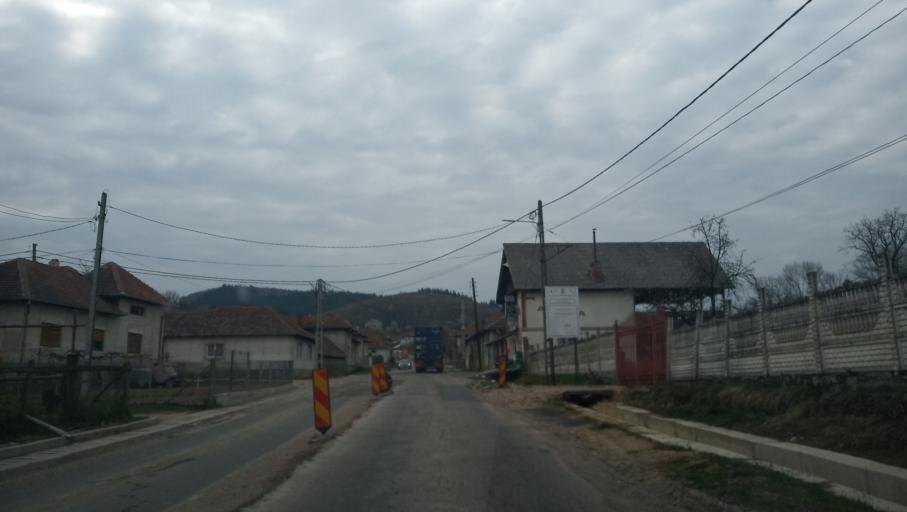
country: RO
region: Bihor
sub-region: Comuna Cristioru de Jos
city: Cristioru de Jos
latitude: 46.4198
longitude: 22.5343
